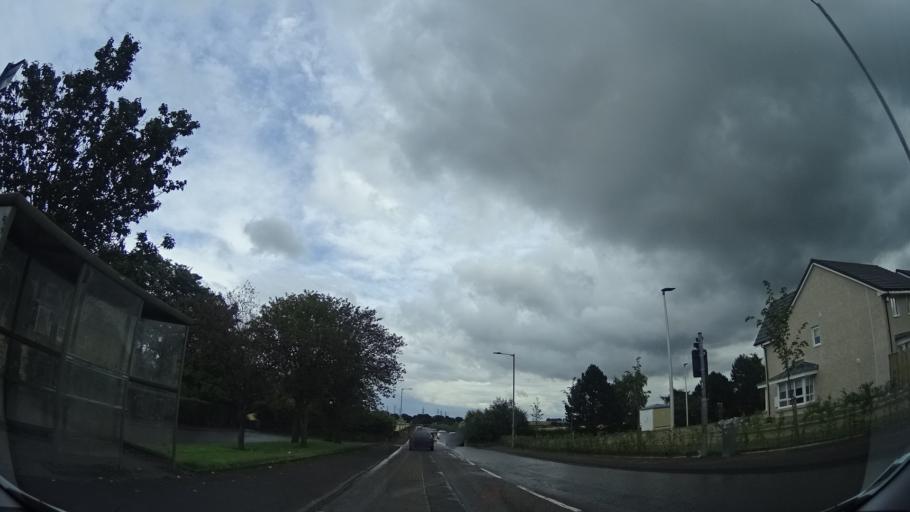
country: GB
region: Scotland
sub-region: Falkirk
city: Bonnybridge
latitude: 56.0046
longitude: -3.8718
